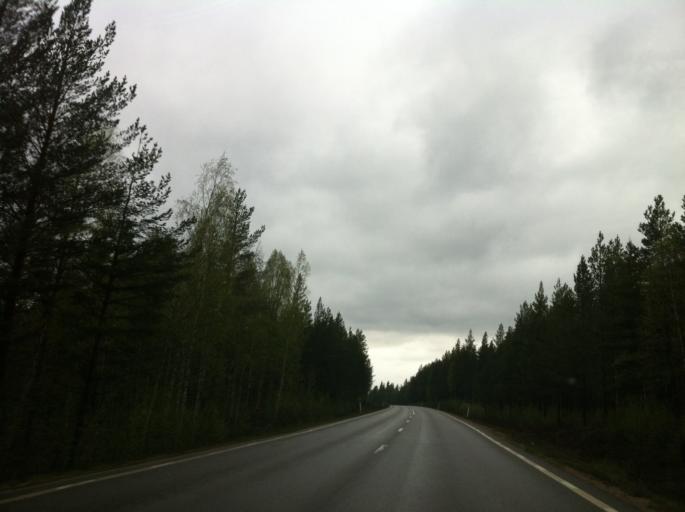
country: SE
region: Jaemtland
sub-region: Harjedalens Kommun
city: Sveg
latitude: 62.1256
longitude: 14.1467
